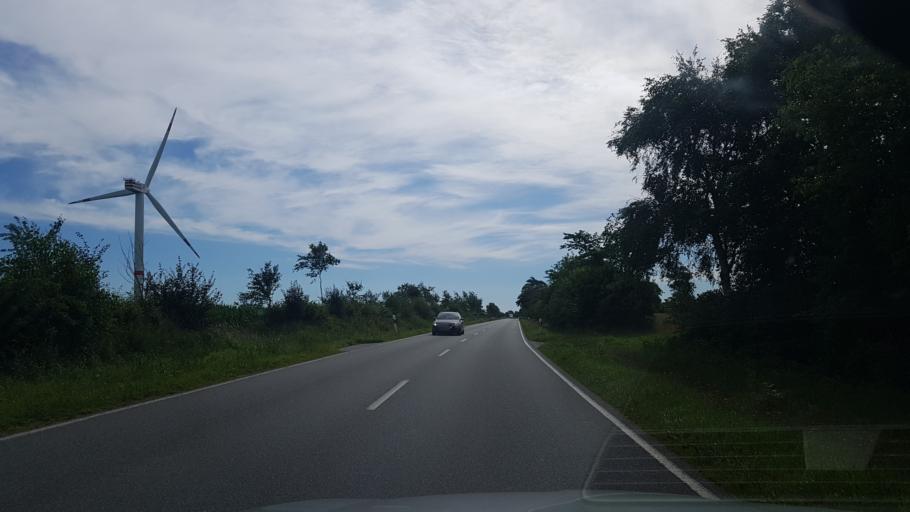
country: DE
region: Schleswig-Holstein
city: Westre
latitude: 54.8829
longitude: 8.9949
